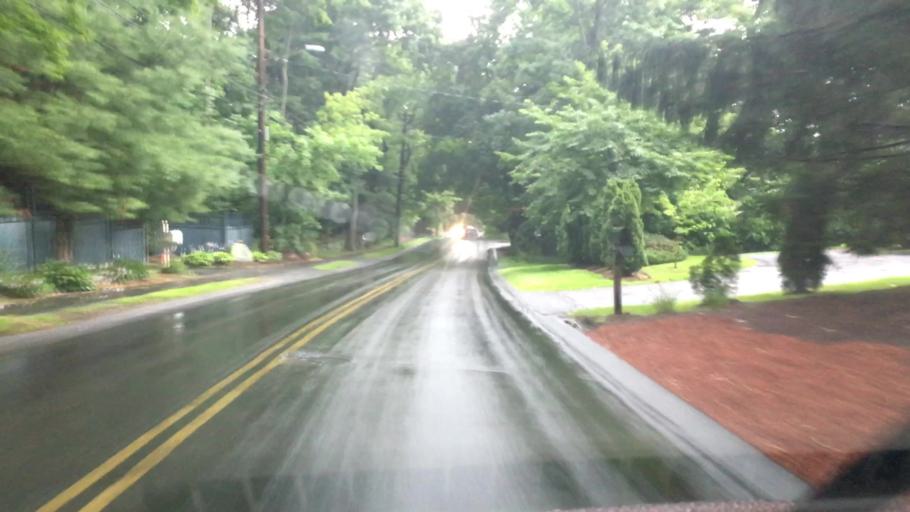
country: US
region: Massachusetts
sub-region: Middlesex County
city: Lexington
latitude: 42.4632
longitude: -71.2186
